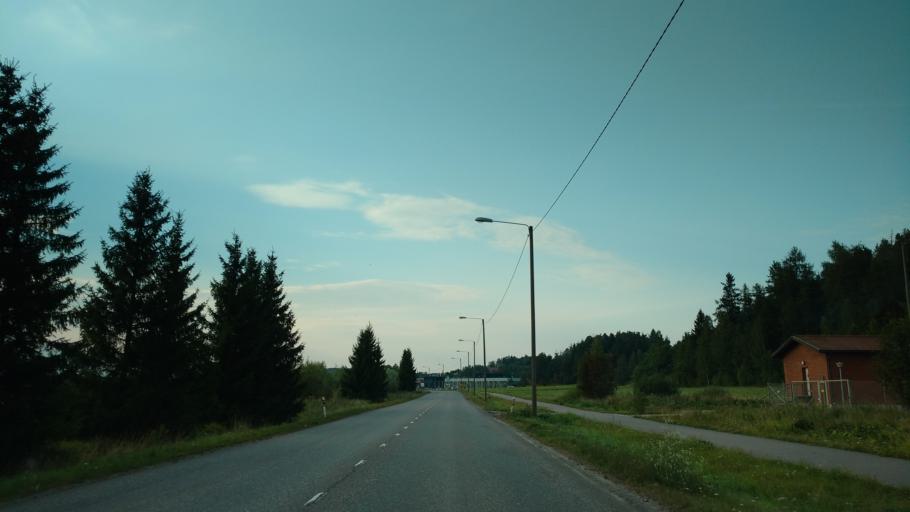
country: FI
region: Varsinais-Suomi
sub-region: Salo
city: Halikko
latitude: 60.3878
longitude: 23.0961
